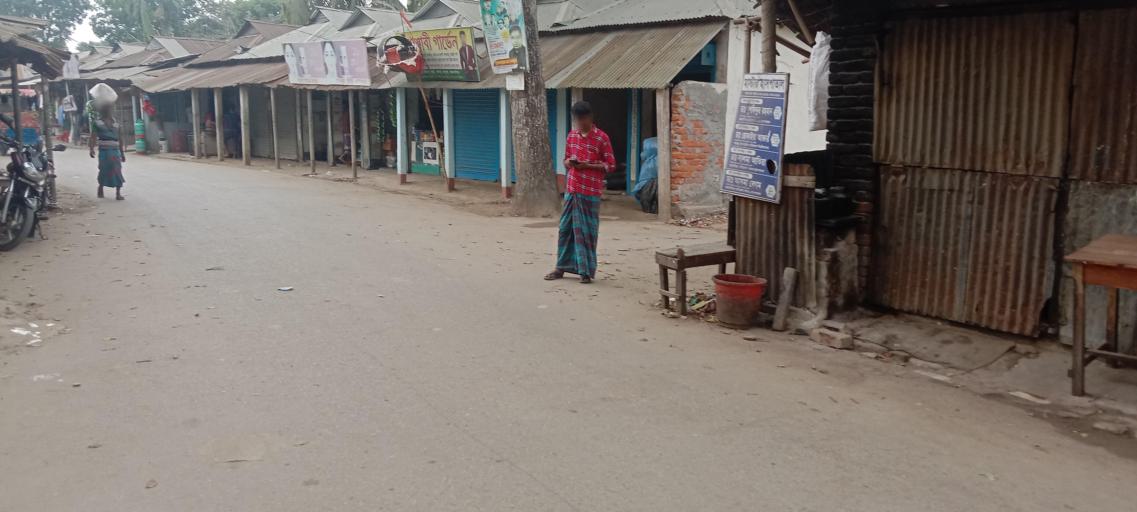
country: BD
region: Dhaka
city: Gafargaon
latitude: 24.4617
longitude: 90.4105
